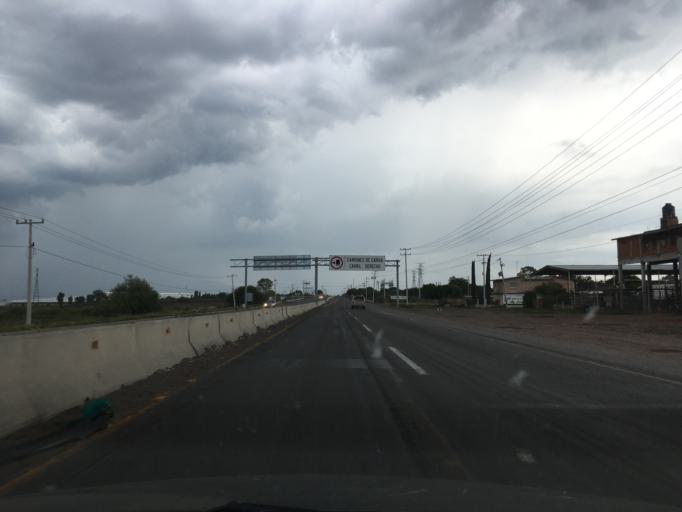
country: MX
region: Guanajuato
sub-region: Celaya
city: El Sauz (El Sauz de Villasenor)
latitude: 20.3796
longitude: -100.7945
